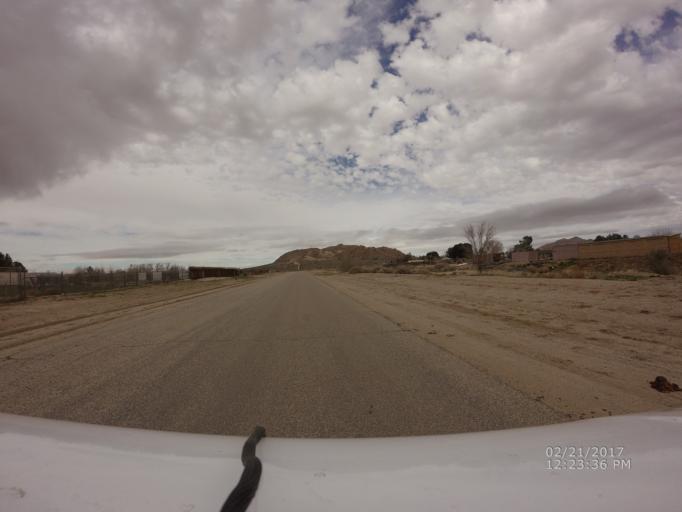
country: US
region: California
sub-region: Los Angeles County
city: Lake Los Angeles
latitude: 34.6366
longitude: -117.8539
